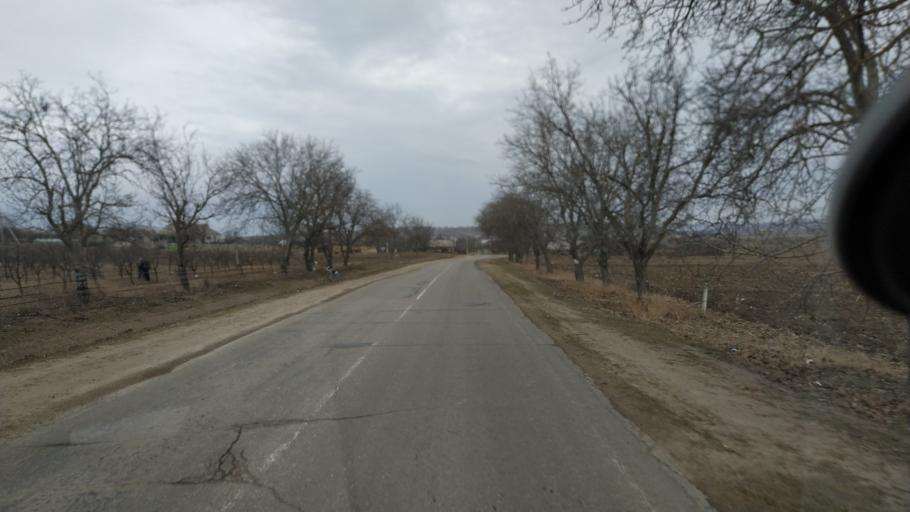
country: MD
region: Telenesti
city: Dubasari
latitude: 47.2442
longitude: 29.1428
